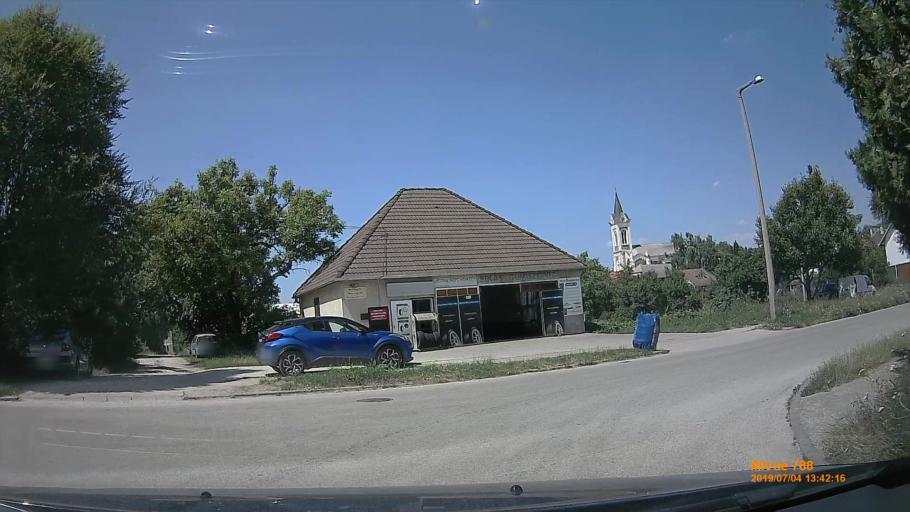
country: HU
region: Komarom-Esztergom
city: Tatabanya
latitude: 47.5733
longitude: 18.3837
